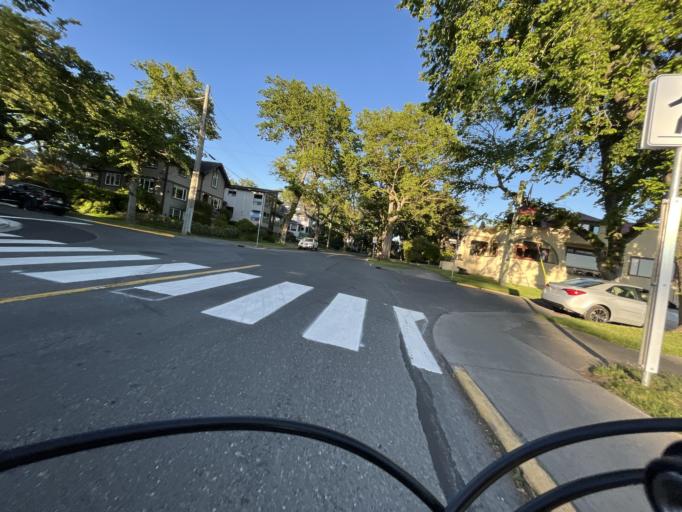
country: CA
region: British Columbia
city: Victoria
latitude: 48.4101
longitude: -123.3365
